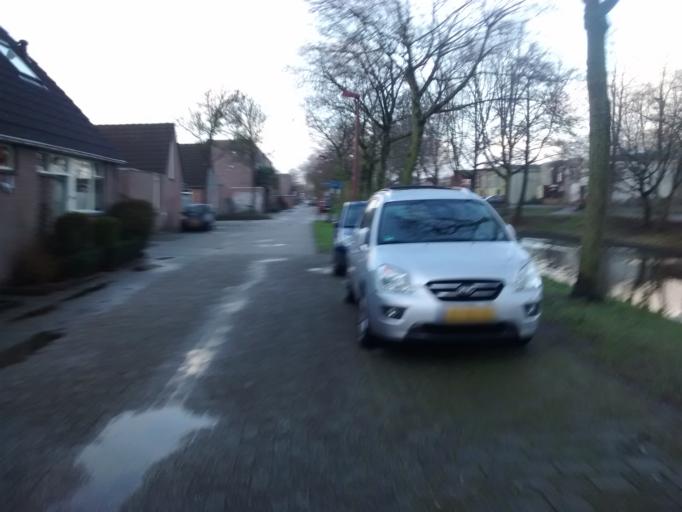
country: NL
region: Utrecht
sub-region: Gemeente Vianen
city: Vianen
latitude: 52.0121
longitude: 5.0911
